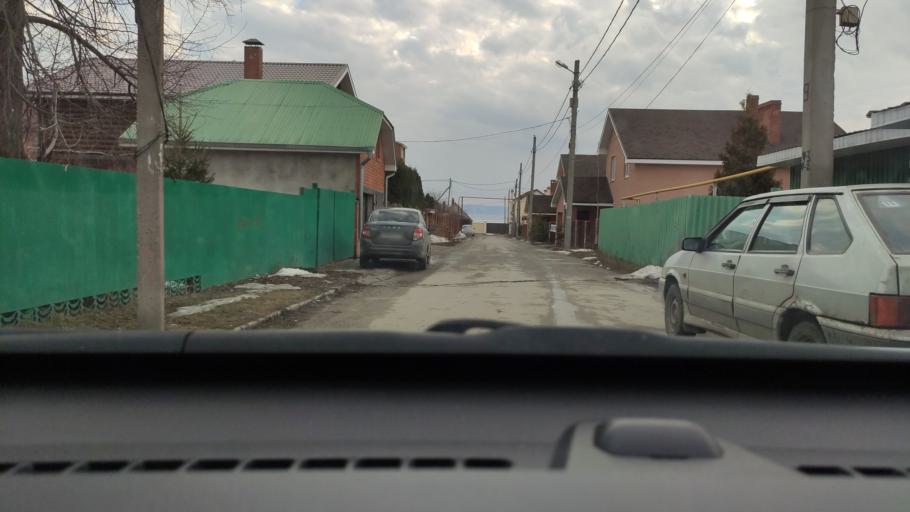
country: RU
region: Samara
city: Podstepki
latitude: 53.5083
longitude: 49.2394
